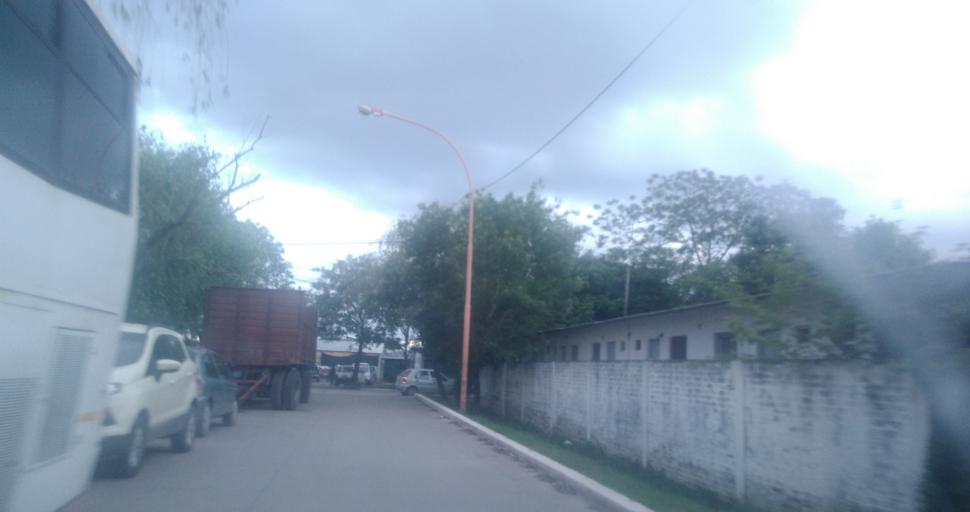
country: AR
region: Chaco
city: Resistencia
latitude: -27.4557
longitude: -58.9752
